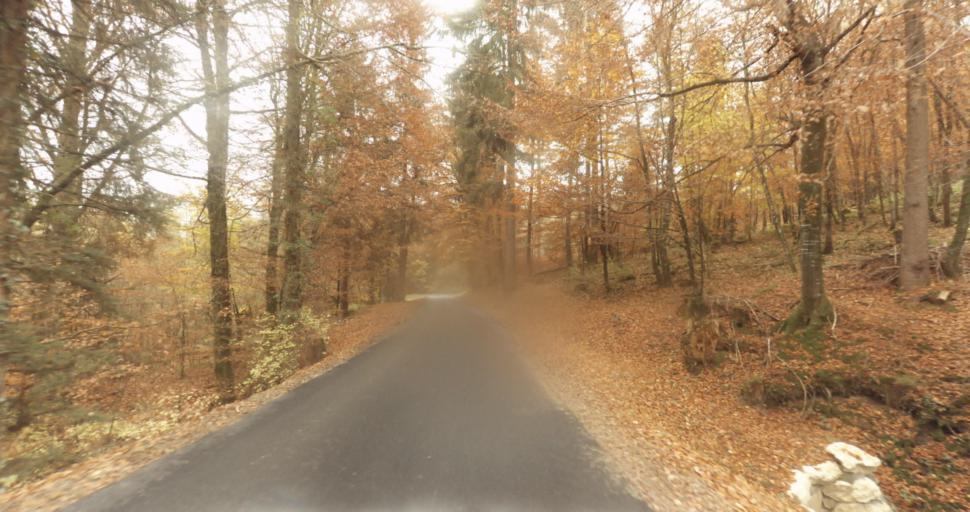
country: FR
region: Rhone-Alpes
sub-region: Departement de la Haute-Savoie
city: Saint-Martin-Bellevue
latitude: 45.9893
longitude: 6.1444
